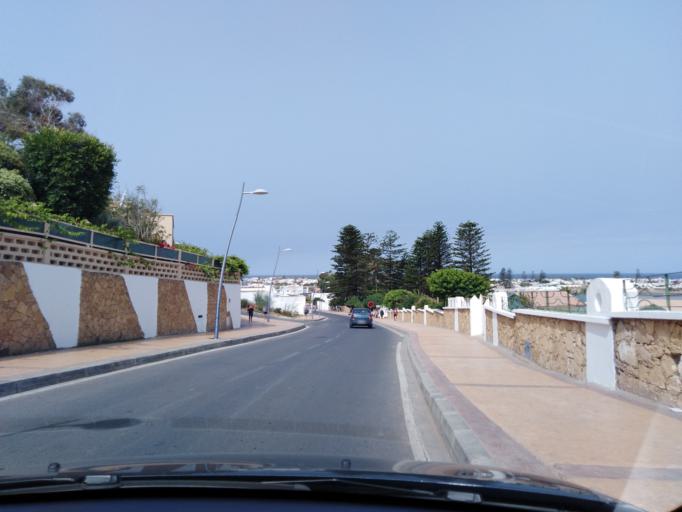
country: MA
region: Doukkala-Abda
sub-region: Safi
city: Safi
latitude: 32.7337
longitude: -9.0366
